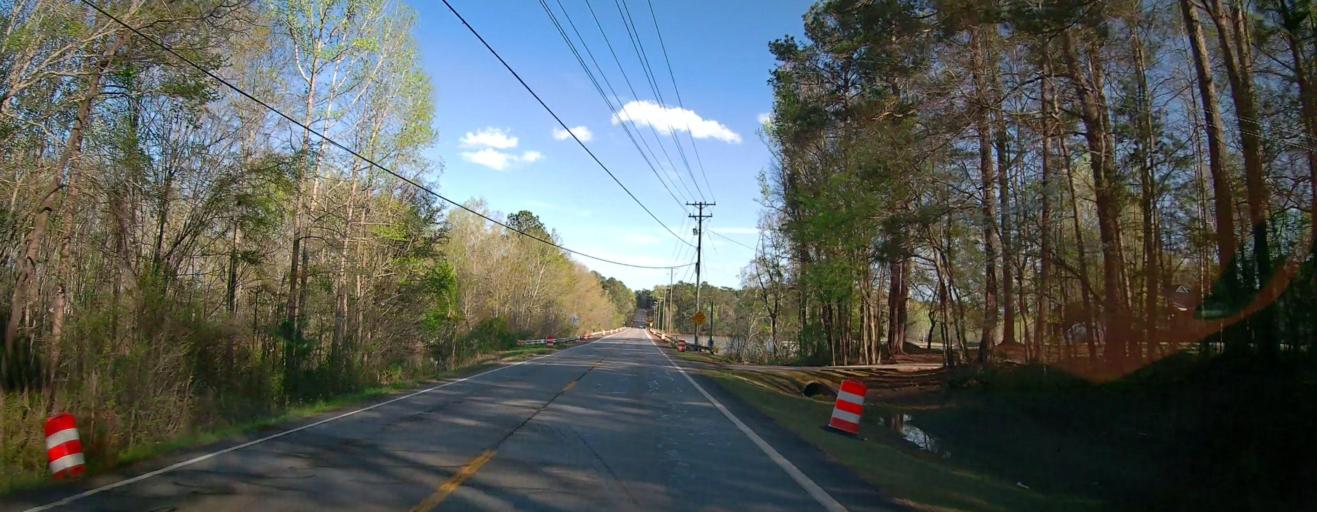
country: US
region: Georgia
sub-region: Putnam County
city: Eatonton
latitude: 33.1650
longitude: -83.3784
